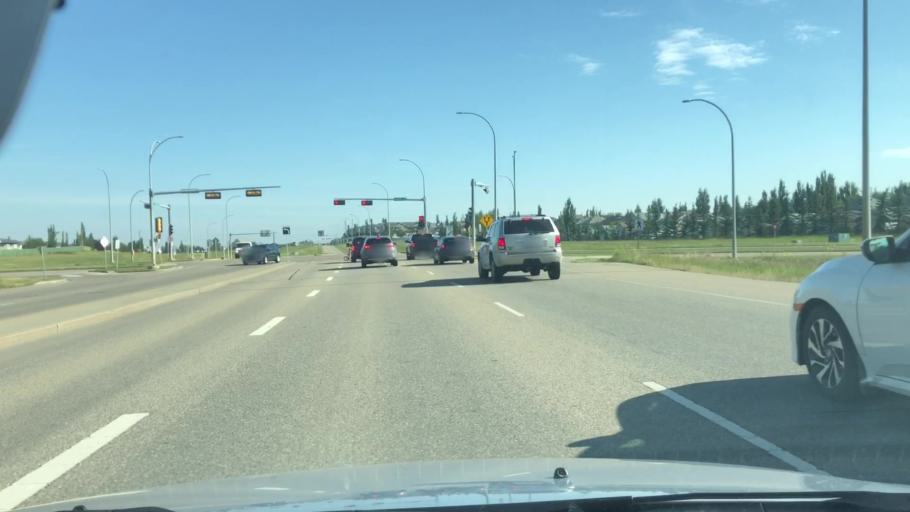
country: CA
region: Alberta
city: Edmonton
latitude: 53.4507
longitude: -113.5900
